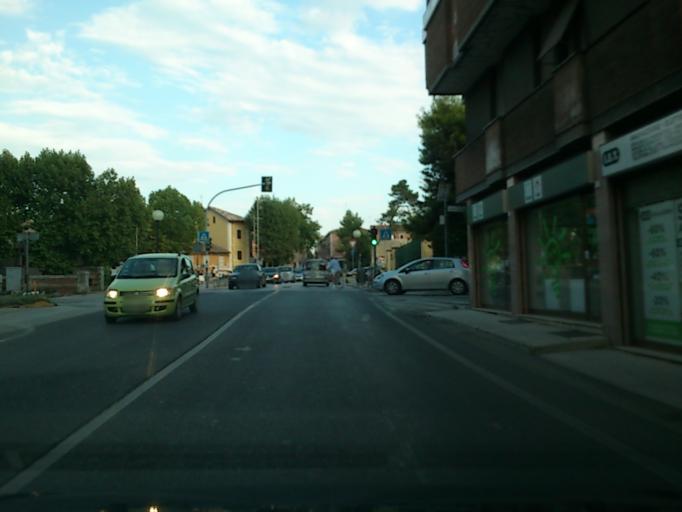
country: IT
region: The Marches
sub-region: Provincia di Pesaro e Urbino
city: Fano
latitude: 43.8470
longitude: 13.0118
